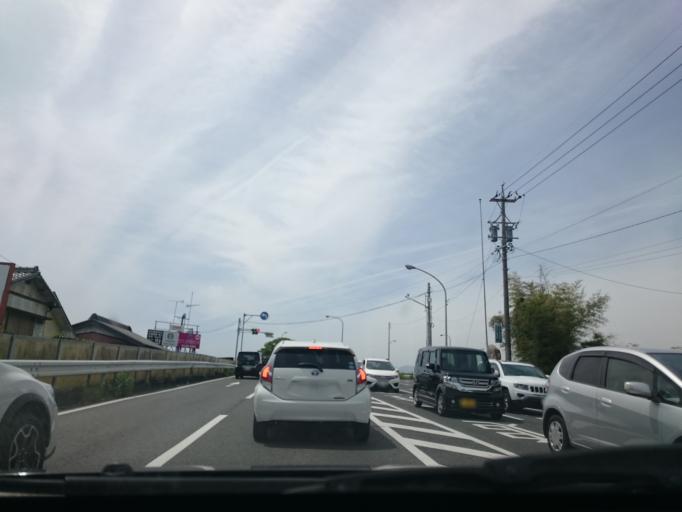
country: JP
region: Mie
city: Yokkaichi
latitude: 34.9758
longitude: 136.6038
